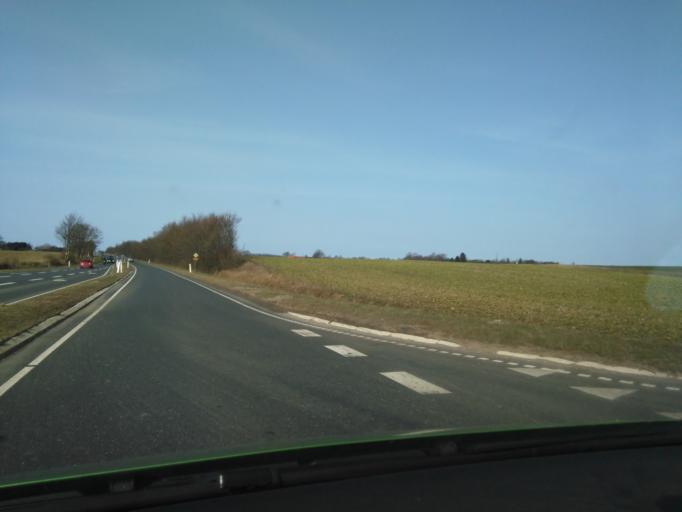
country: DK
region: Central Jutland
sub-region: Silkeborg Kommune
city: Kjellerup
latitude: 56.2571
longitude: 9.4433
